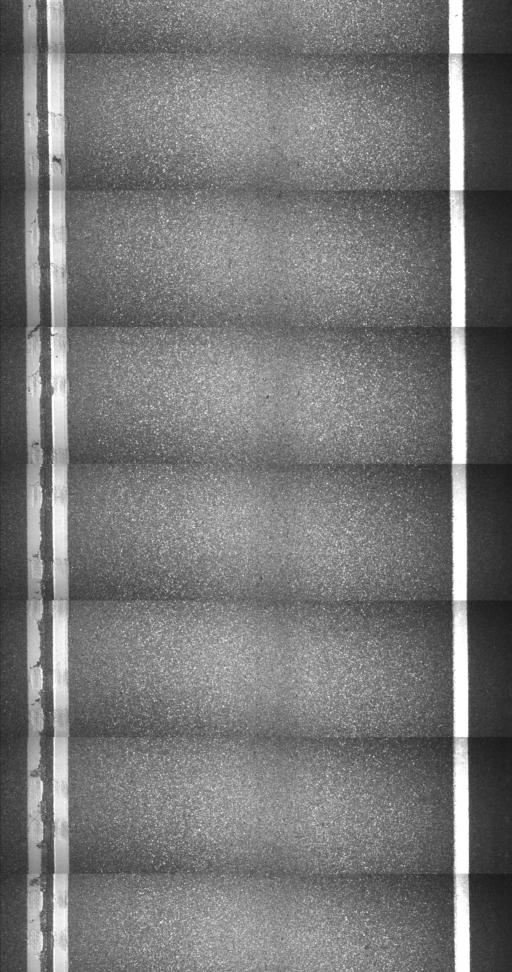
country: US
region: Vermont
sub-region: Orange County
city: Randolph
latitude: 43.7635
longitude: -72.7429
